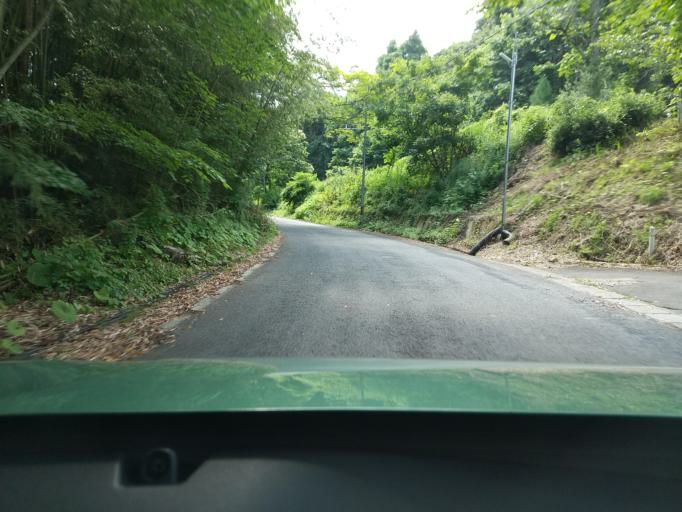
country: JP
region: Iwate
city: Ichinoseki
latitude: 39.0069
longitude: 141.2169
